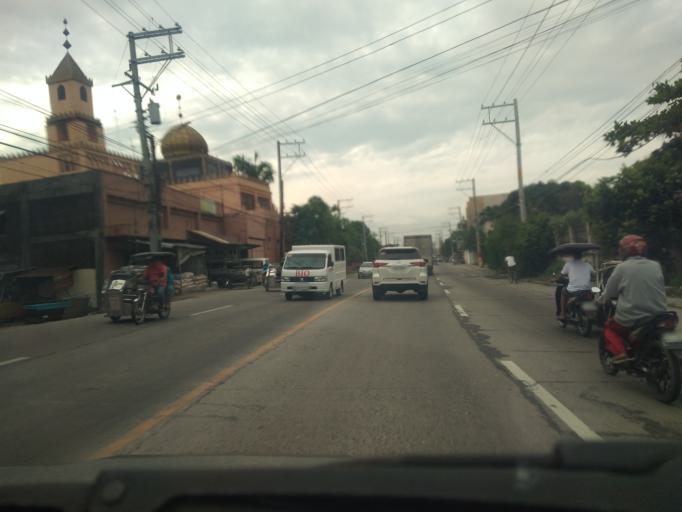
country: PH
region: Central Luzon
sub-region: Province of Pampanga
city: Del Pilar
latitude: 15.0315
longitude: 120.6965
